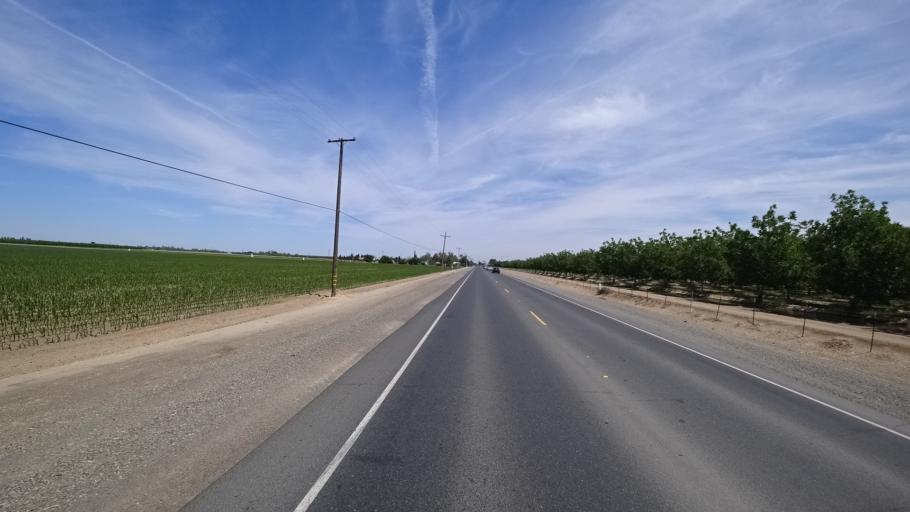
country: US
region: California
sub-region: Kings County
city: Hanford
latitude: 36.3358
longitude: -119.6010
